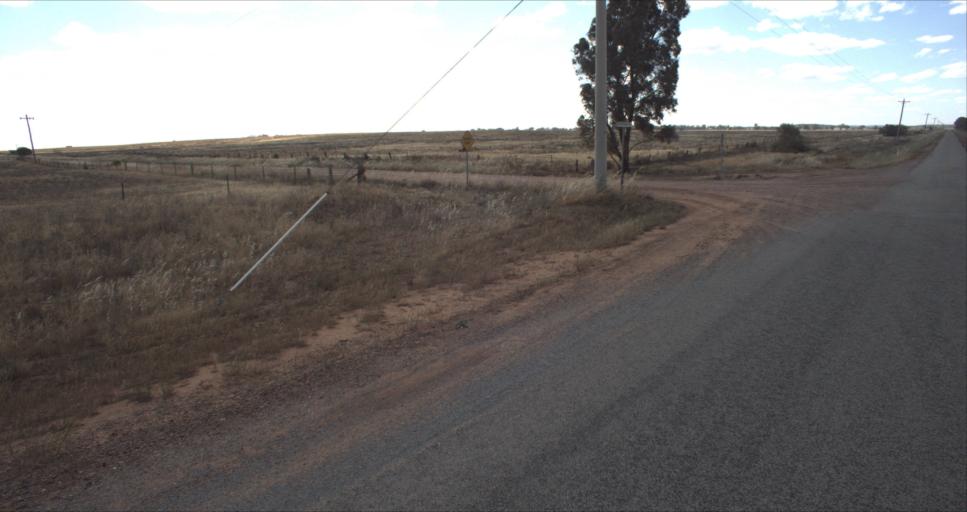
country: AU
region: New South Wales
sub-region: Leeton
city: Leeton
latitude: -34.4828
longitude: 146.2488
